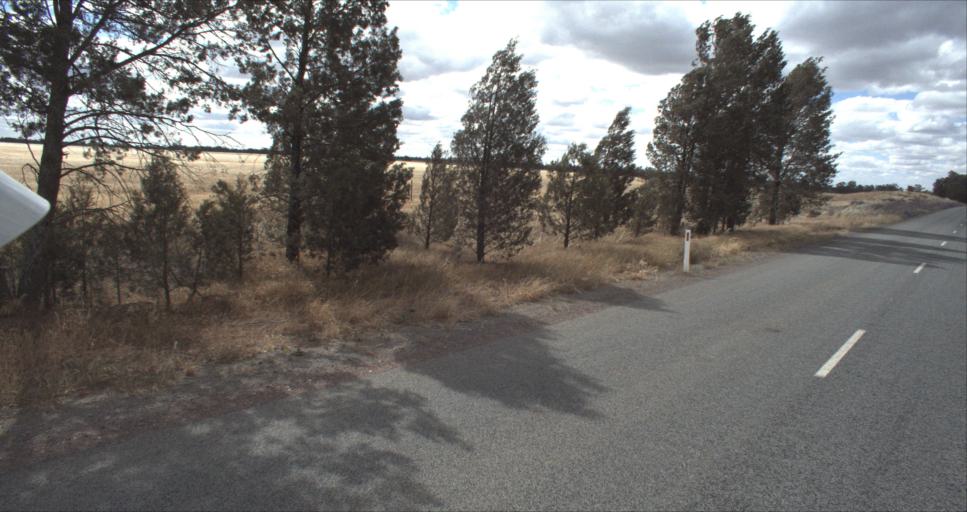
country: AU
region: New South Wales
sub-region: Leeton
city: Leeton
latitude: -34.6754
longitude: 146.3466
